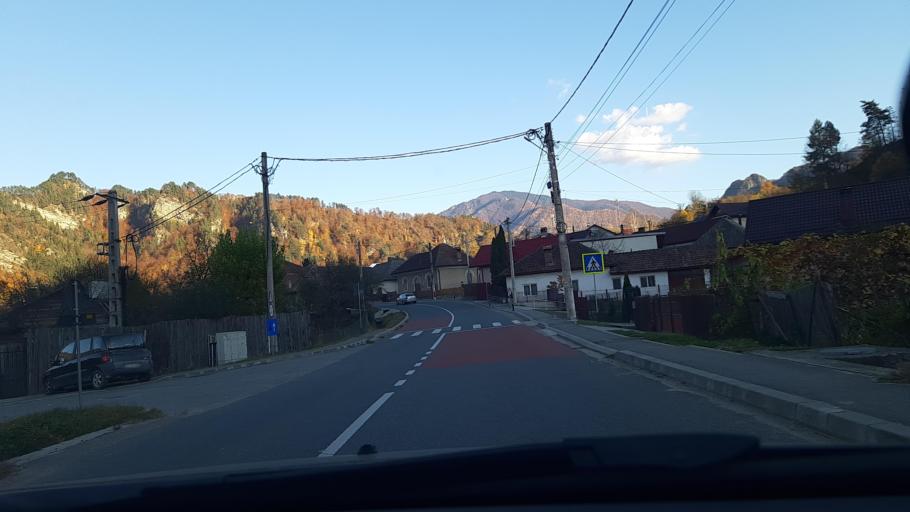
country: RO
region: Valcea
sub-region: Comuna Brezoi
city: Brezoi
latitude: 45.3439
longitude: 24.2360
